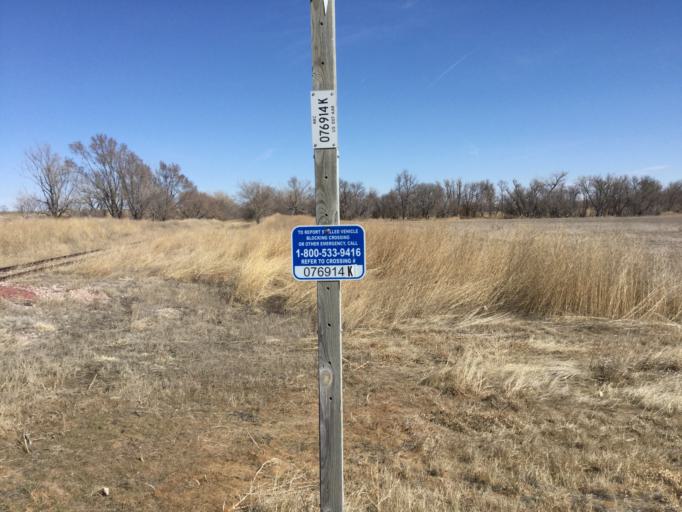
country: US
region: Kansas
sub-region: Decatur County
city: Oberlin
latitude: 39.9065
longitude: -100.7772
